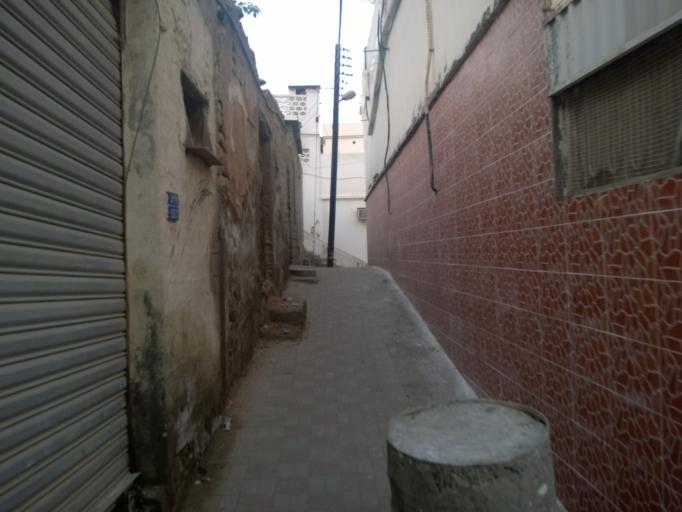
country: OM
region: Muhafazat Masqat
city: Muscat
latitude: 23.6197
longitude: 58.5620
